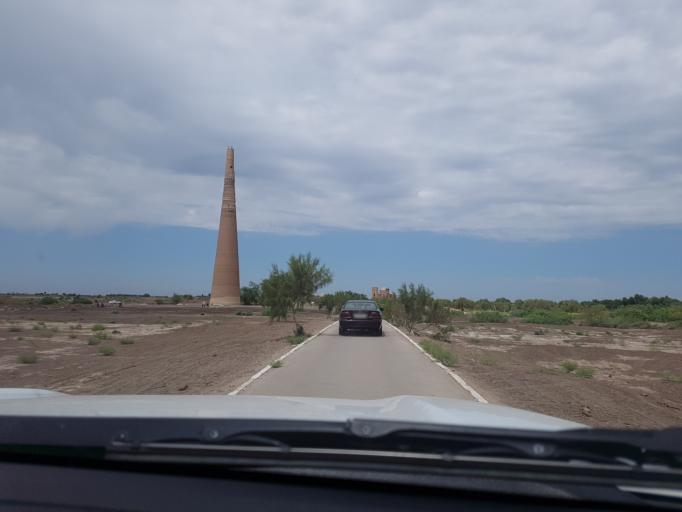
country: TM
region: Dasoguz
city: Koeneuergench
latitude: 42.3084
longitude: 59.1443
